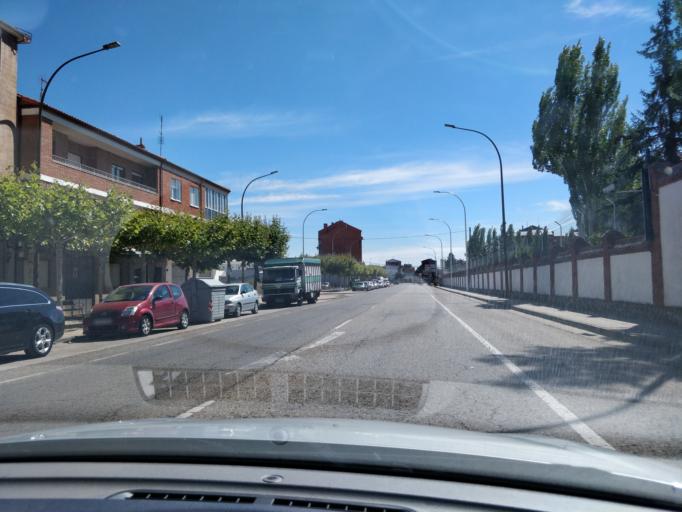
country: ES
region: Castille and Leon
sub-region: Provincia de Leon
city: Astorga
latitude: 42.4616
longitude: -6.0675
